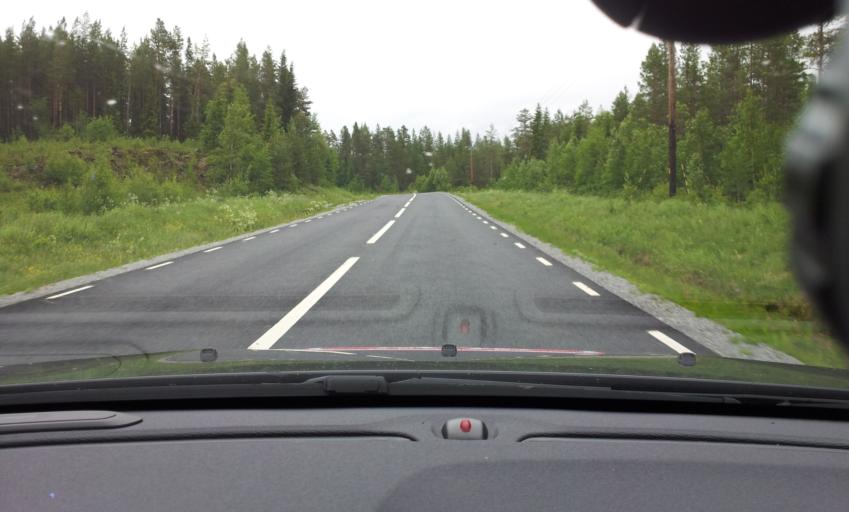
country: SE
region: Jaemtland
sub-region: OEstersunds Kommun
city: Lit
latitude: 63.7380
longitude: 14.7727
